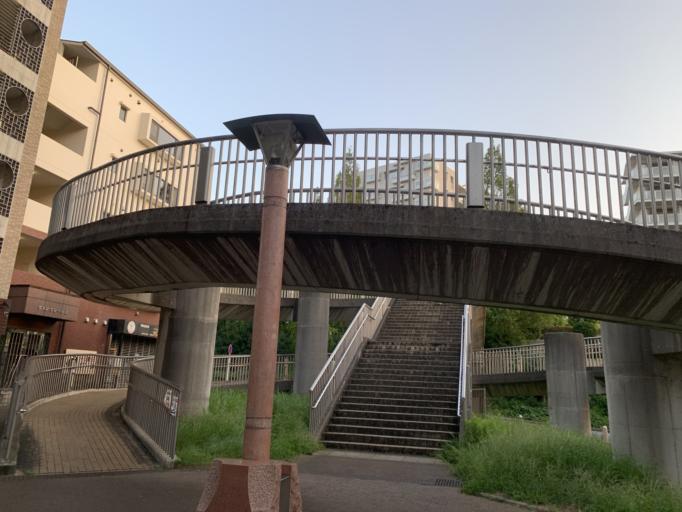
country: JP
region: Tokyo
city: Chofugaoka
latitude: 35.5598
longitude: 139.5918
